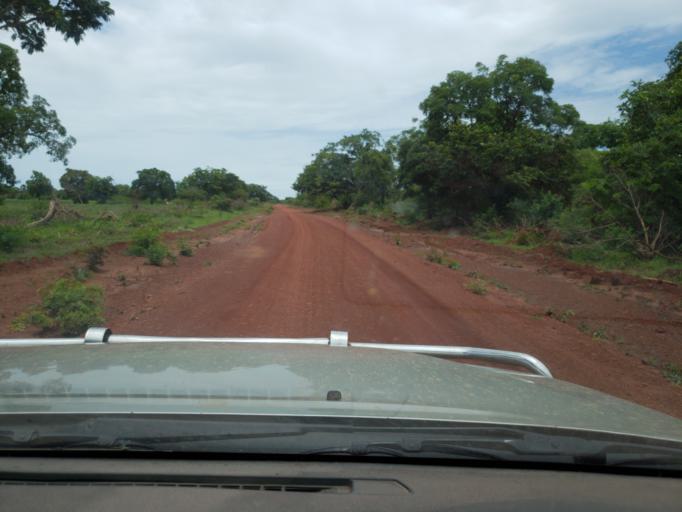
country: ML
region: Sikasso
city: Sikasso
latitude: 11.6578
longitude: -6.3421
